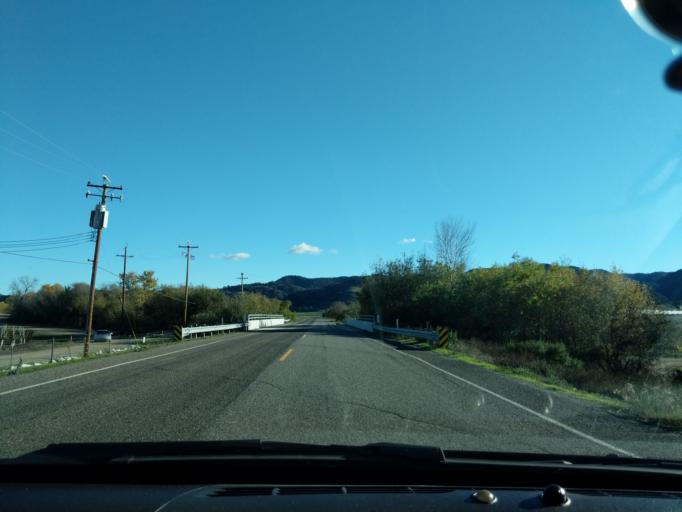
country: US
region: California
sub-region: Santa Barbara County
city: Los Alamos
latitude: 34.7504
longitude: -120.2917
